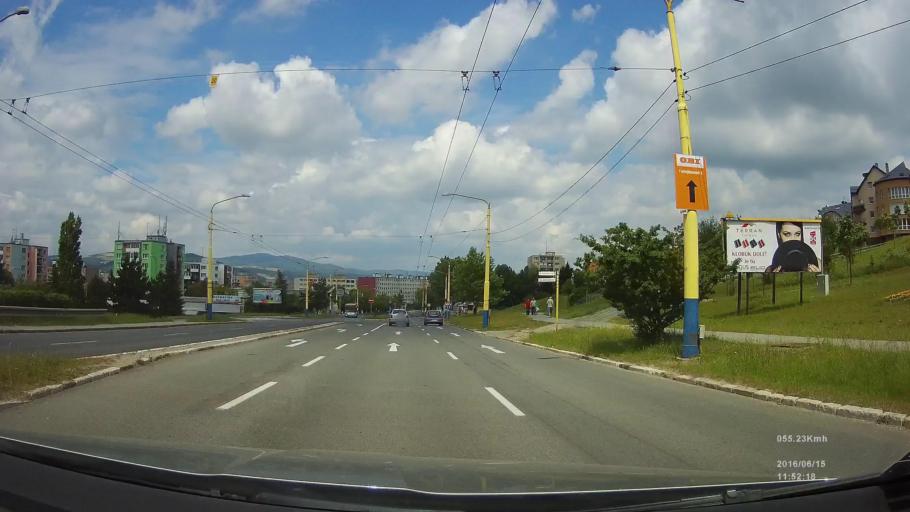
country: SK
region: Kosicky
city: Kosice
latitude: 48.7372
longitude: 21.2832
